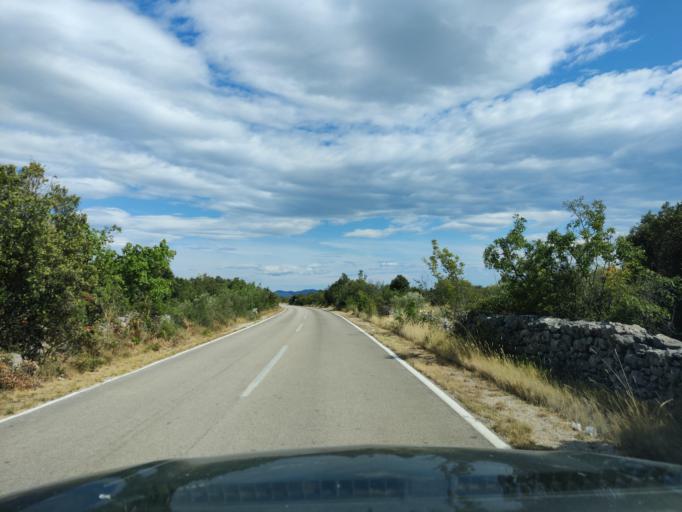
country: HR
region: Sibensko-Kniniska
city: Zaton
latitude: 43.7479
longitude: 15.8437
